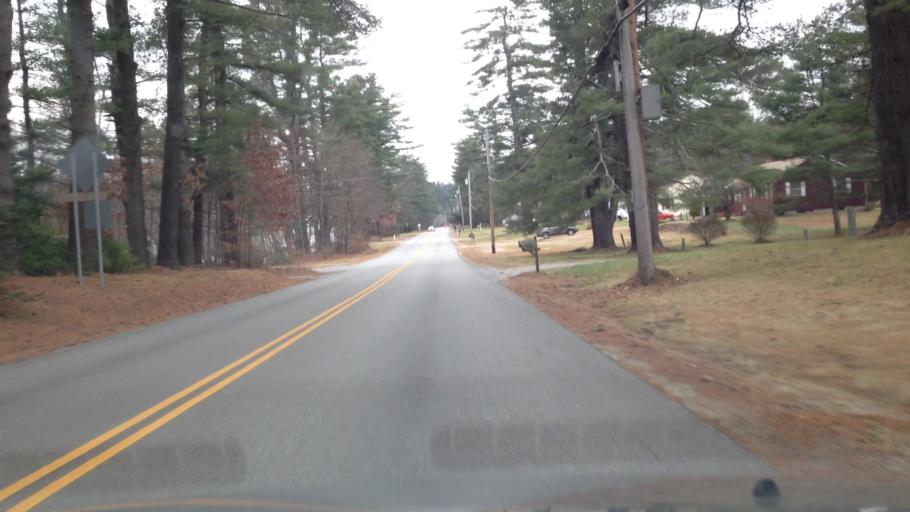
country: US
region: New Hampshire
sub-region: Cheshire County
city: Swanzey
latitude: 42.8844
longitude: -72.2844
